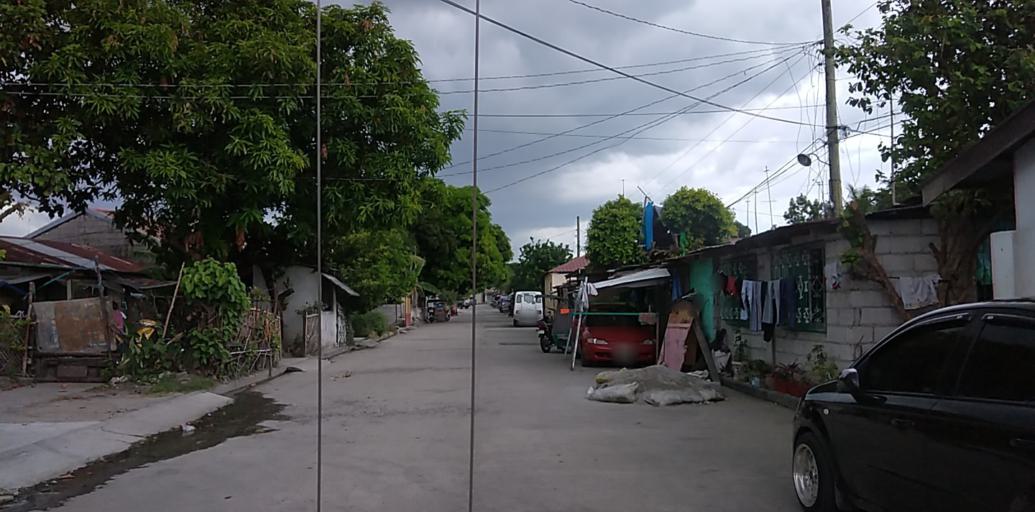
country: PH
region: Central Luzon
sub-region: Province of Pampanga
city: Pio
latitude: 15.0428
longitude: 120.5319
